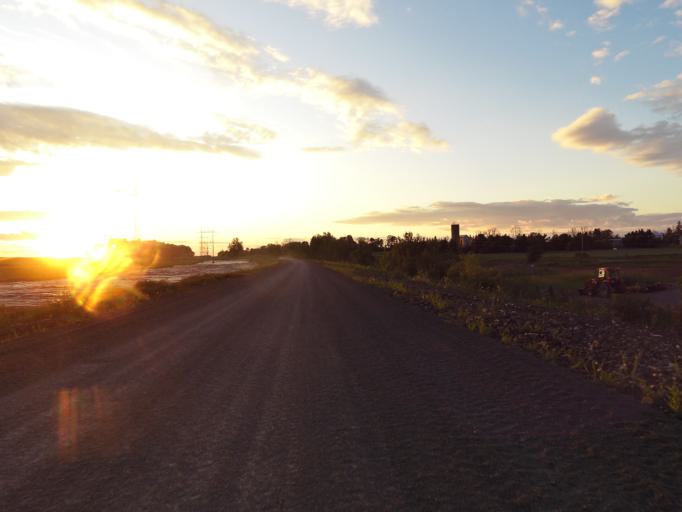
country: CA
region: Ontario
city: Arnprior
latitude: 45.4031
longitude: -76.3253
